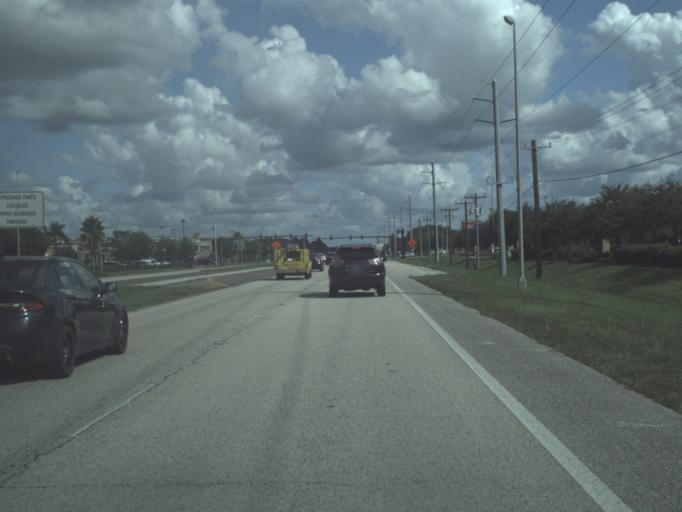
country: US
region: Florida
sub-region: Sarasota County
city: North Port
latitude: 27.0369
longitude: -82.2163
